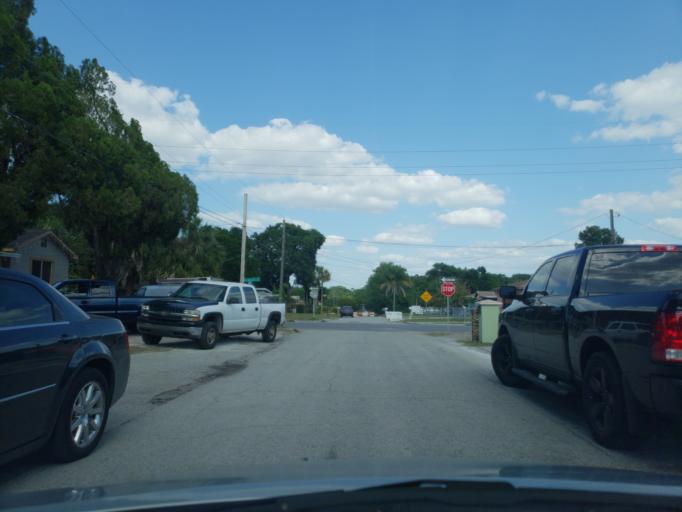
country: US
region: Florida
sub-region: Hillsborough County
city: Tampa
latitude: 27.9696
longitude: -82.4832
